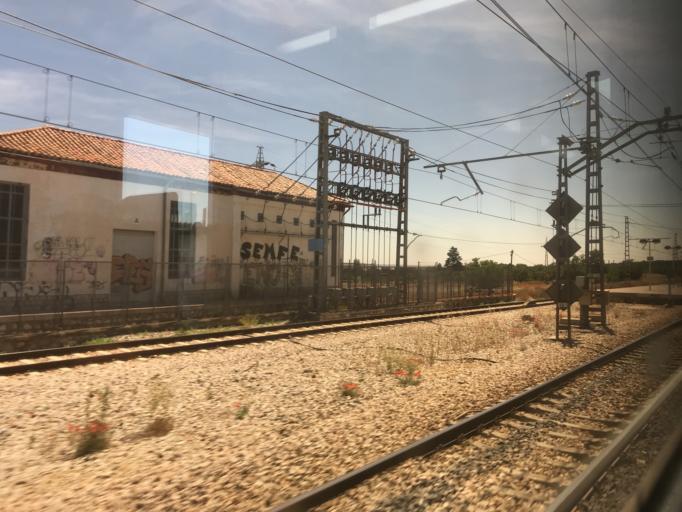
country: ES
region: Madrid
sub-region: Provincia de Madrid
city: Valdemoro
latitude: 40.1978
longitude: -3.6659
